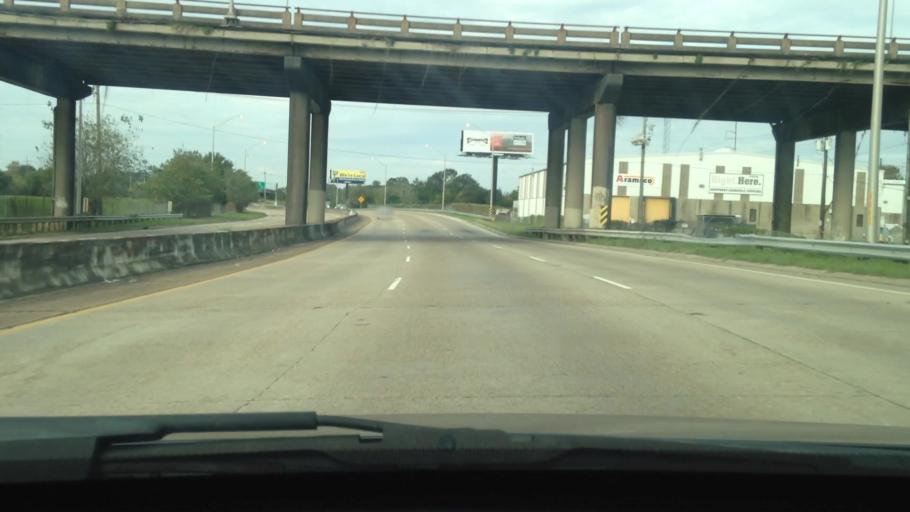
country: US
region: Louisiana
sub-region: Jefferson Parish
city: Jefferson
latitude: 29.9718
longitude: -90.1560
